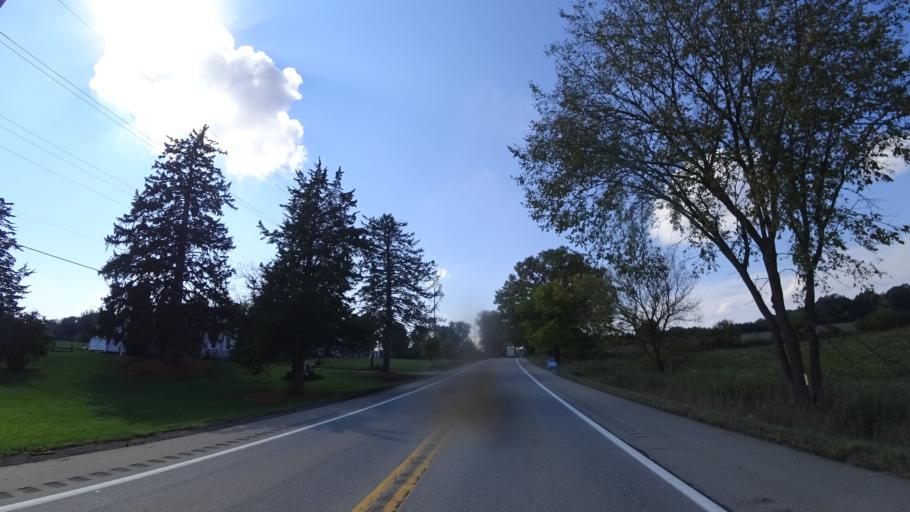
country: US
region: Michigan
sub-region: Jackson County
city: Concord
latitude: 42.1651
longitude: -84.6768
